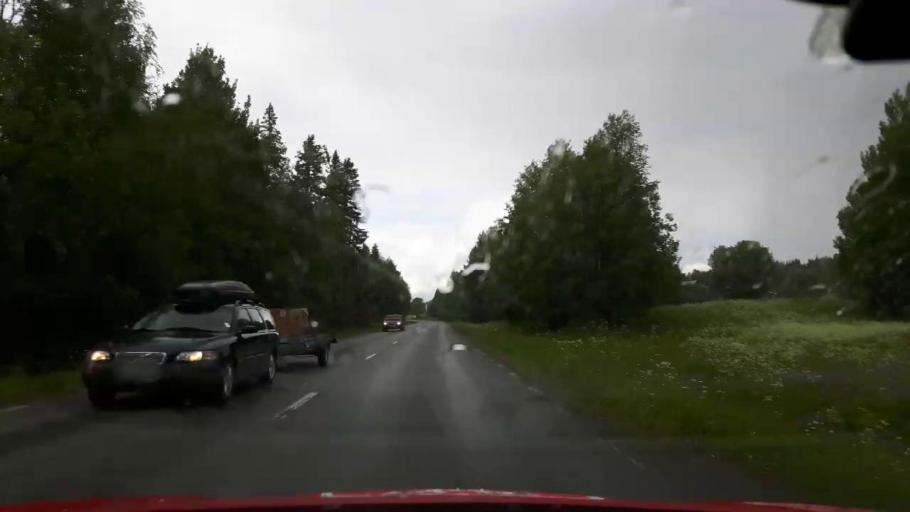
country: SE
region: Jaemtland
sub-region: Krokoms Kommun
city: Krokom
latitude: 63.4470
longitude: 14.1956
